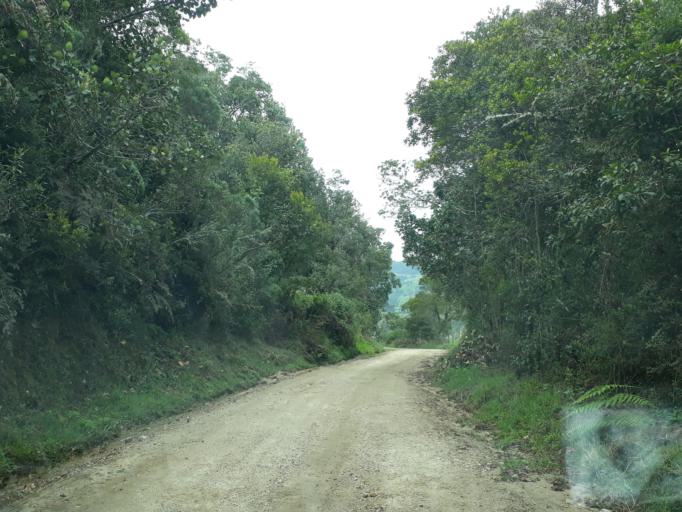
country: CO
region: Cundinamarca
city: Villapinzon
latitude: 5.1578
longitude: -73.5359
